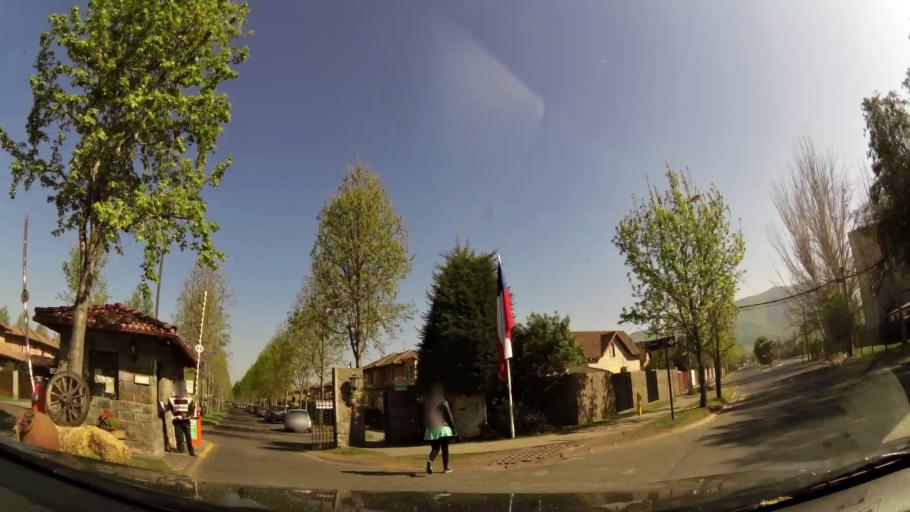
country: CL
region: Santiago Metropolitan
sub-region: Provincia de Chacabuco
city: Chicureo Abajo
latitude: -33.3590
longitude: -70.6762
